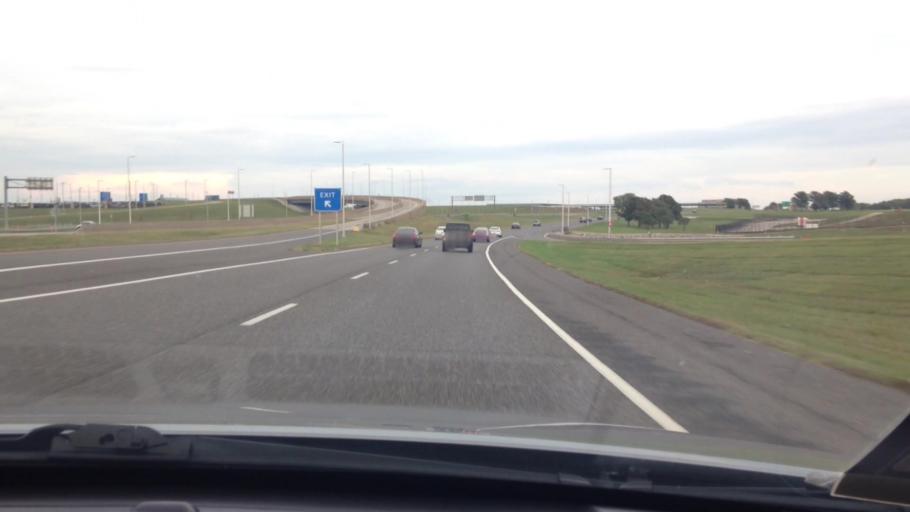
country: US
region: Missouri
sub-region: Platte County
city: Weatherby Lake
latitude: 39.3094
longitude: -94.7055
